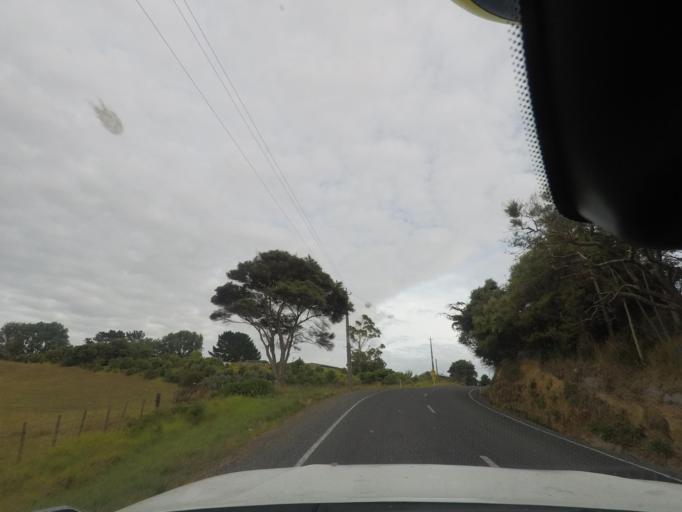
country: NZ
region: Auckland
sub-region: Auckland
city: Parakai
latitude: -36.5288
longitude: 174.2937
